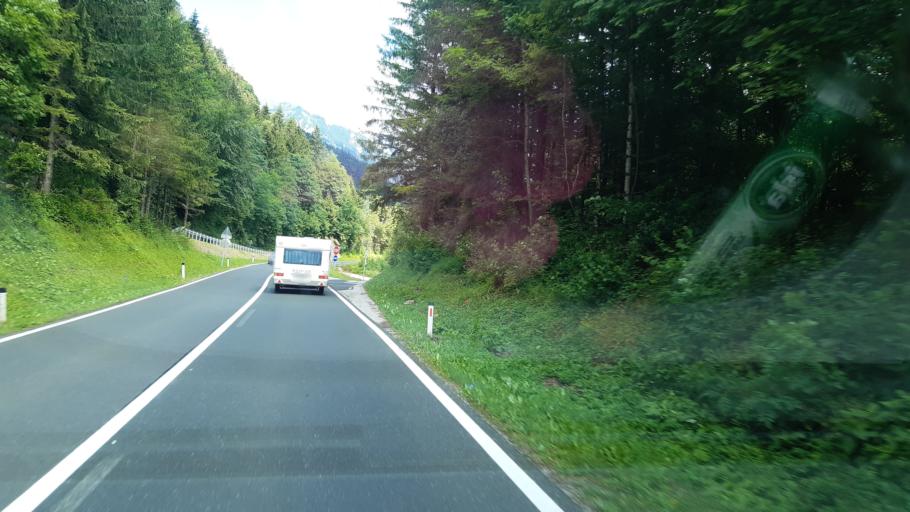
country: SI
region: Trzic
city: Trzic
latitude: 46.3818
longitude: 14.2954
